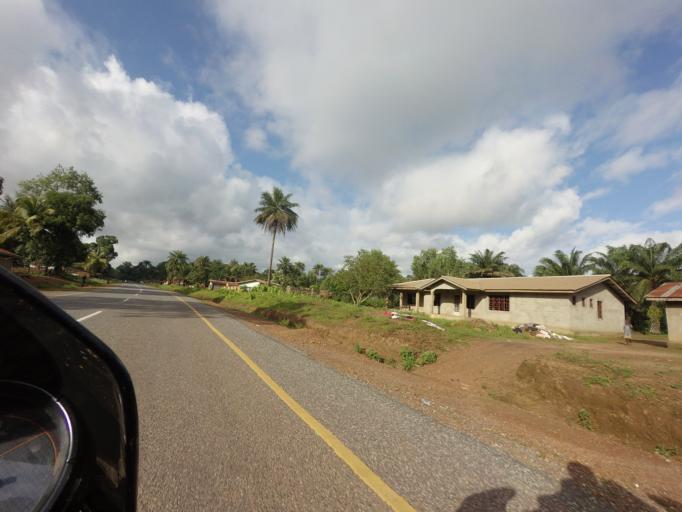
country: SL
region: Northern Province
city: Kambia
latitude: 9.0216
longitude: -12.9438
